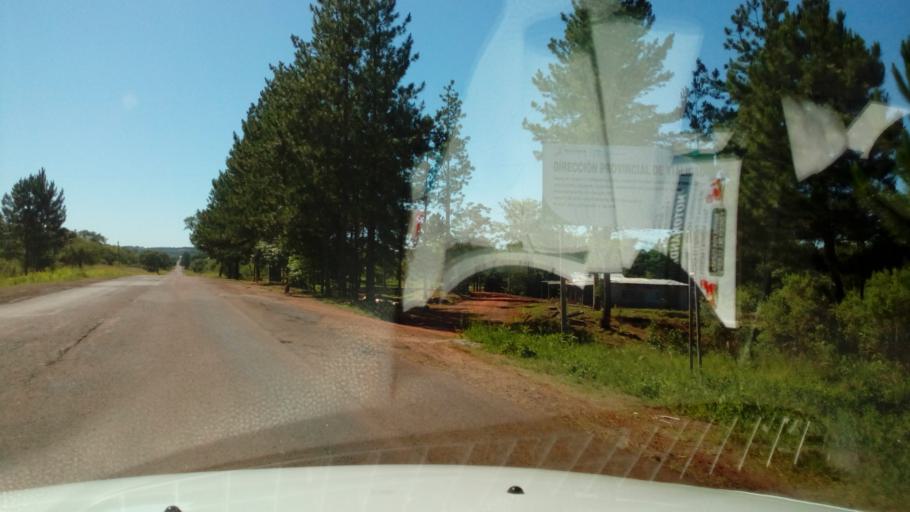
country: AR
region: Misiones
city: Almafuerte
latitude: -27.5628
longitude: -55.4088
